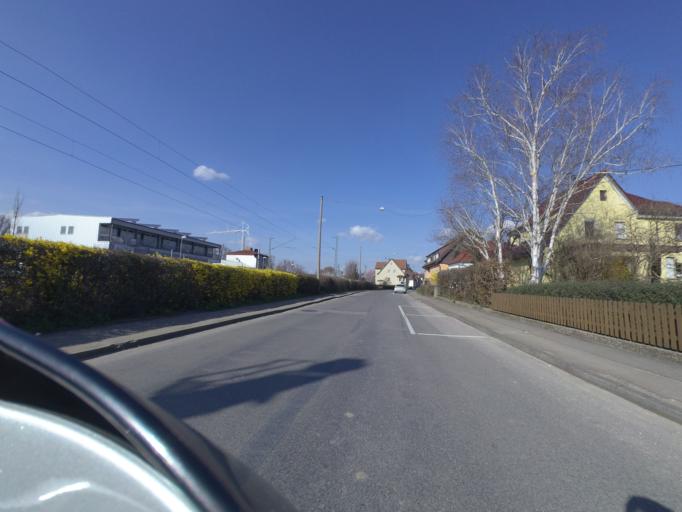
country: DE
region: Baden-Wuerttemberg
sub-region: Regierungsbezirk Stuttgart
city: Oberboihingen
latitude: 48.6520
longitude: 9.3652
